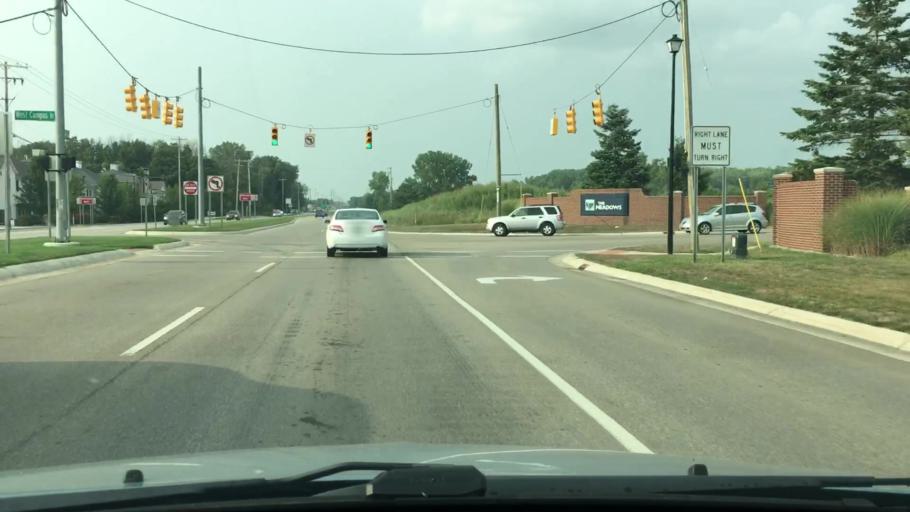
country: US
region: Michigan
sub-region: Ottawa County
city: Allendale
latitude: 42.9631
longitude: -85.9040
